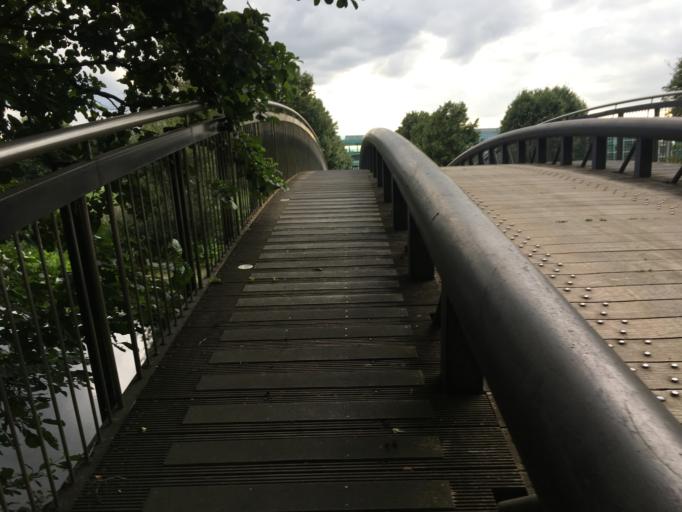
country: GB
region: England
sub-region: Royal Borough of Windsor and Maidenhead
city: Datchet
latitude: 51.4903
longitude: -0.5635
